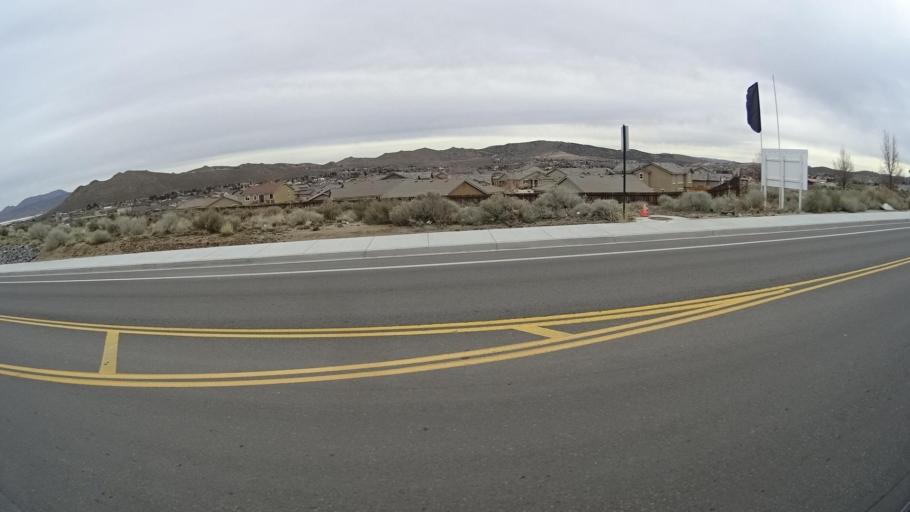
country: US
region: Nevada
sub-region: Washoe County
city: Golden Valley
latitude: 39.6073
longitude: -119.8439
